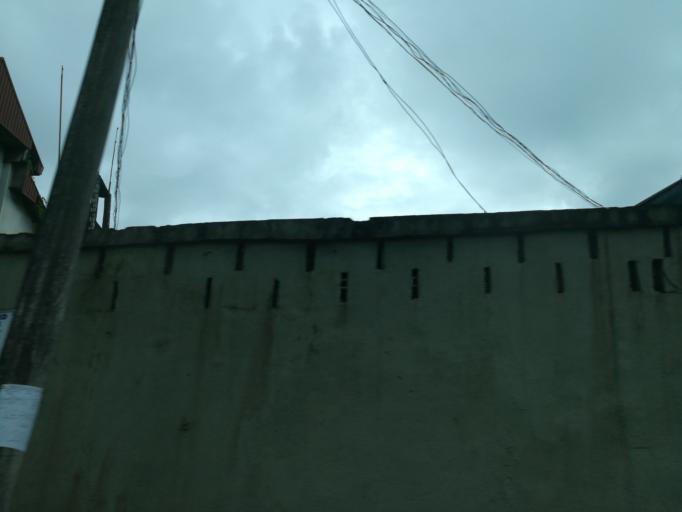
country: NG
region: Rivers
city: Port Harcourt
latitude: 4.8387
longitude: 7.0332
